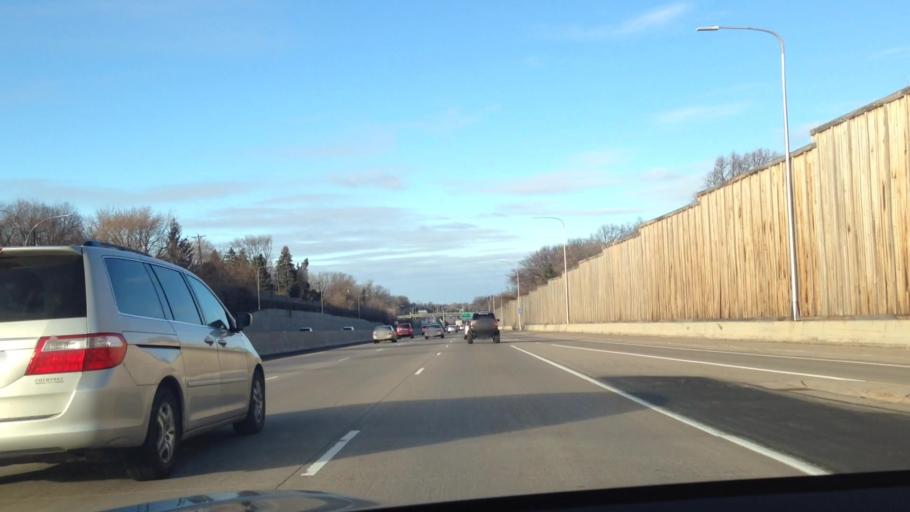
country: US
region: Minnesota
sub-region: Hennepin County
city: Golden Valley
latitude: 45.0028
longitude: -93.3492
